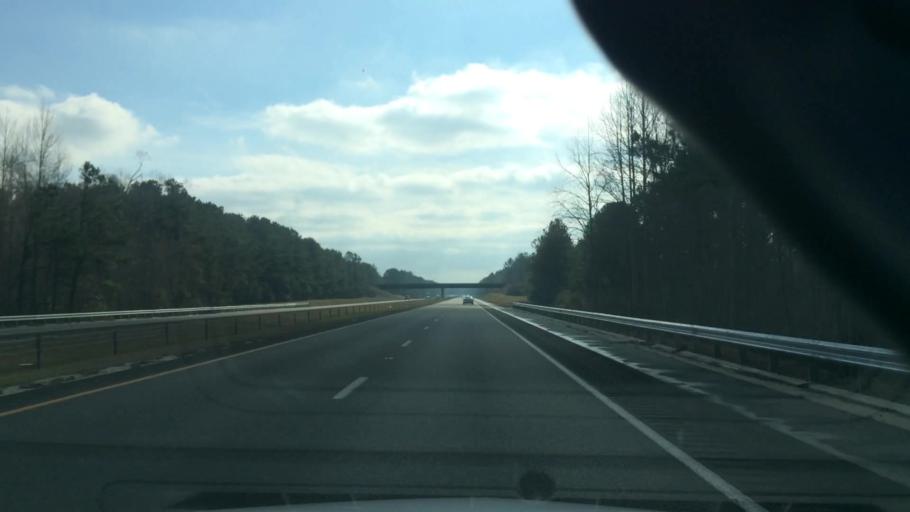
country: US
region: North Carolina
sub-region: Pender County
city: Rocky Point
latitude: 34.4833
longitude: -77.8785
